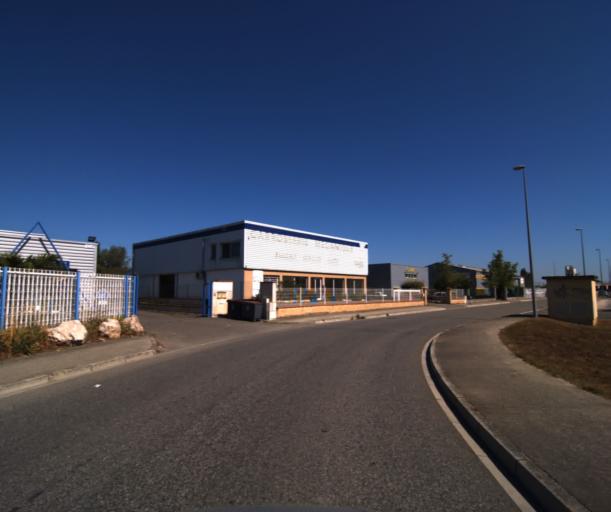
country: FR
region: Midi-Pyrenees
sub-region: Departement de la Haute-Garonne
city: Saubens
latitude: 43.4799
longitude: 1.3323
